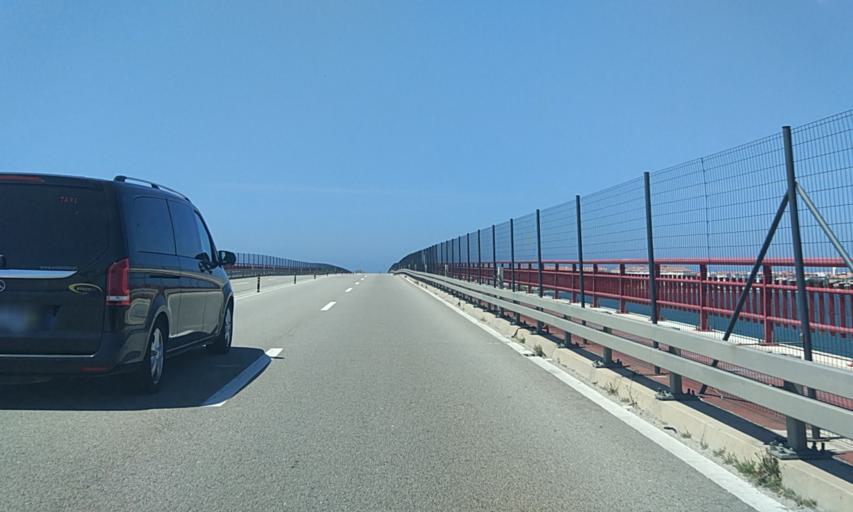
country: PT
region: Aveiro
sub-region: Ilhavo
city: Gafanha da Encarnacao
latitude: 40.6292
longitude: -8.7355
